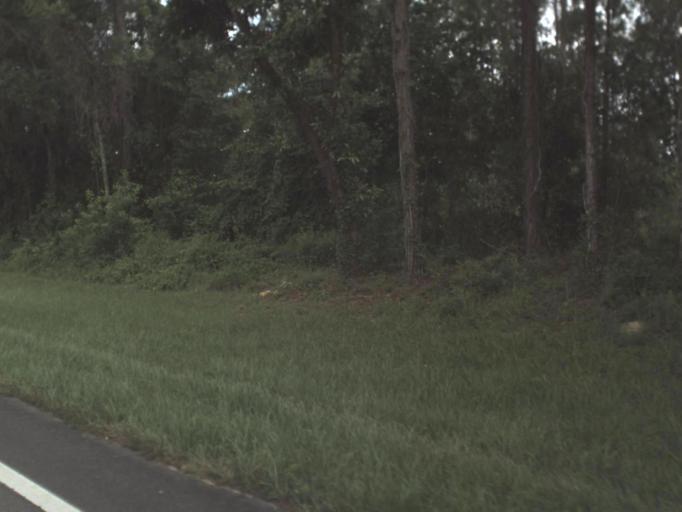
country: US
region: Florida
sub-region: Alachua County
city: Archer
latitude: 29.4650
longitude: -82.4794
